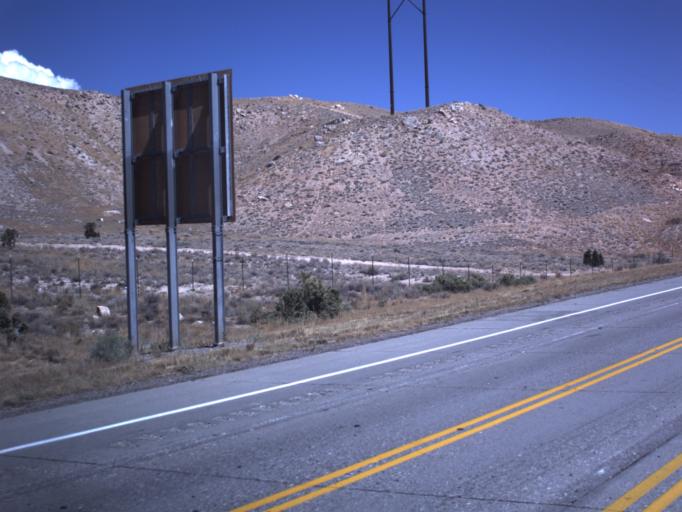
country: US
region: Utah
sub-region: Sevier County
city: Richfield
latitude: 38.7983
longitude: -112.0714
